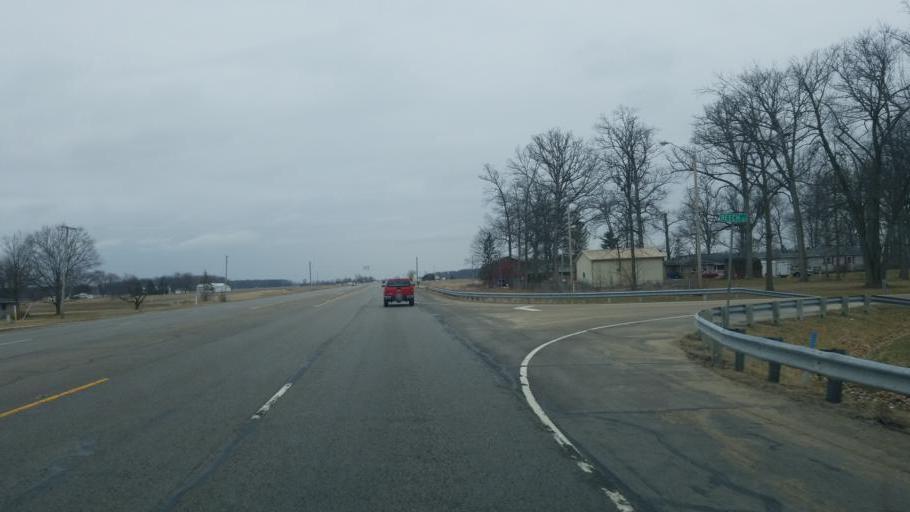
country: US
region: Indiana
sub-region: Adams County
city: Decatur
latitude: 40.7929
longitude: -84.9375
